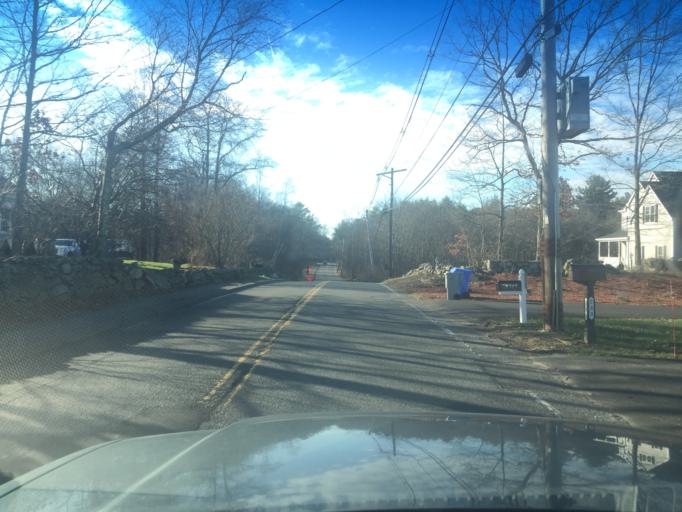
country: US
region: Massachusetts
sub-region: Middlesex County
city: Holliston
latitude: 42.2038
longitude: -71.4564
